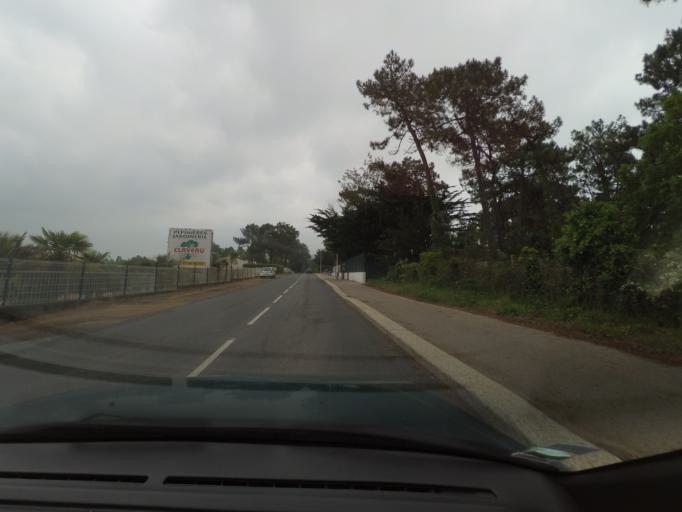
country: FR
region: Pays de la Loire
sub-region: Departement de la Vendee
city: Angles
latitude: 46.3476
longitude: -1.3550
